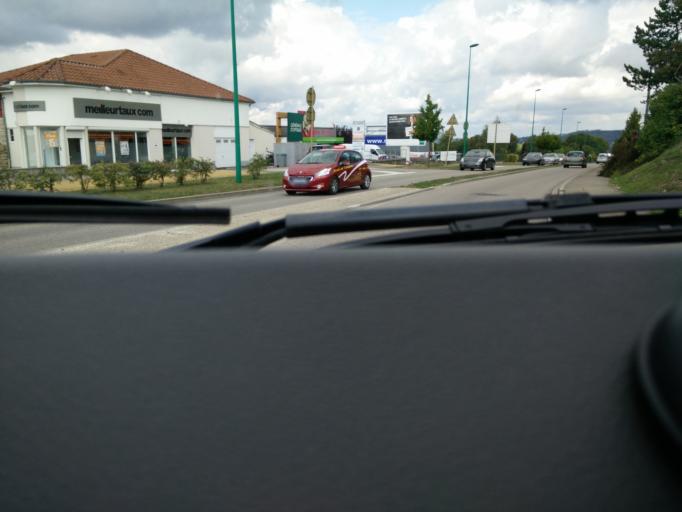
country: FR
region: Lorraine
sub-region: Departement de la Meuse
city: Verdun
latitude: 49.1409
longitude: 5.4105
